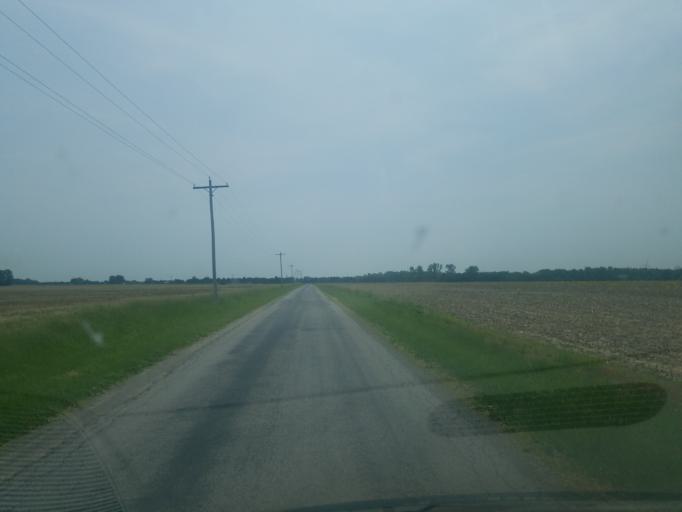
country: US
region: Ohio
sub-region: Wyandot County
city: Upper Sandusky
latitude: 40.7432
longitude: -83.2074
